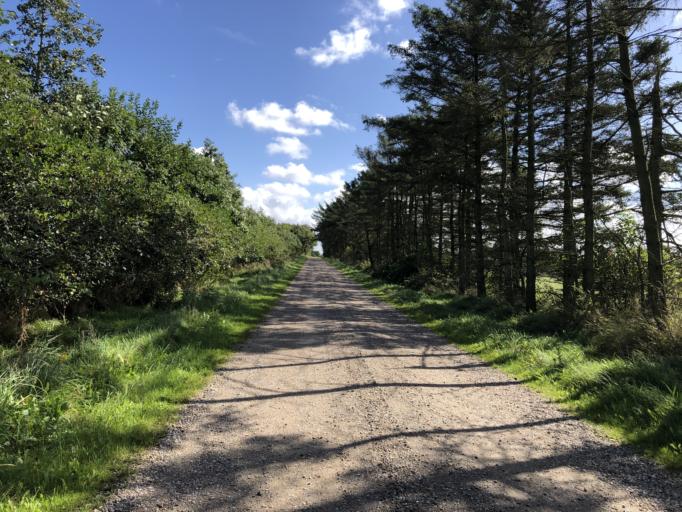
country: DK
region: Central Jutland
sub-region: Holstebro Kommune
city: Ulfborg
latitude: 56.3891
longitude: 8.3583
